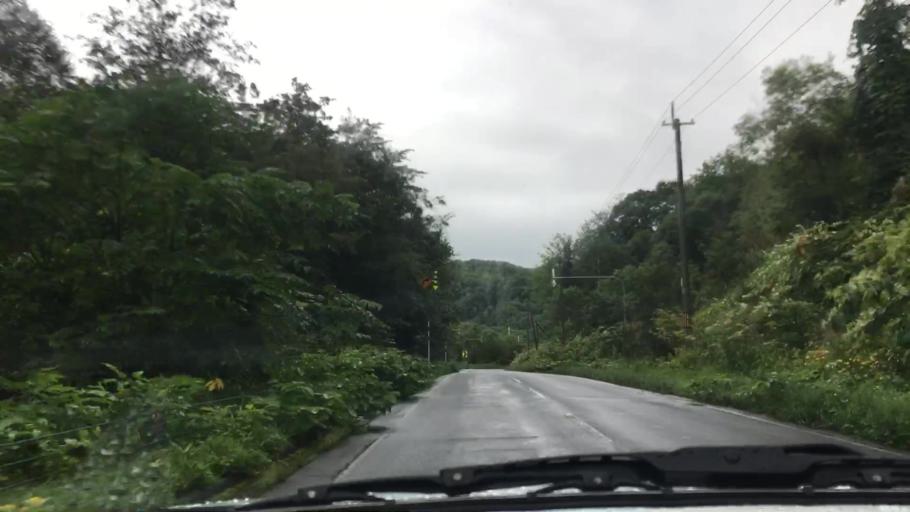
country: JP
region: Hokkaido
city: Niseko Town
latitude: 42.6680
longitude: 140.7774
